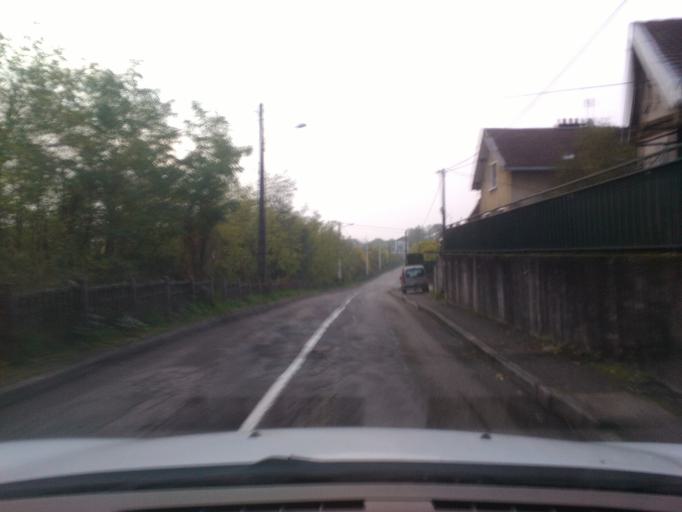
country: FR
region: Lorraine
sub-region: Departement des Vosges
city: Mirecourt
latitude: 48.3033
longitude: 6.1276
